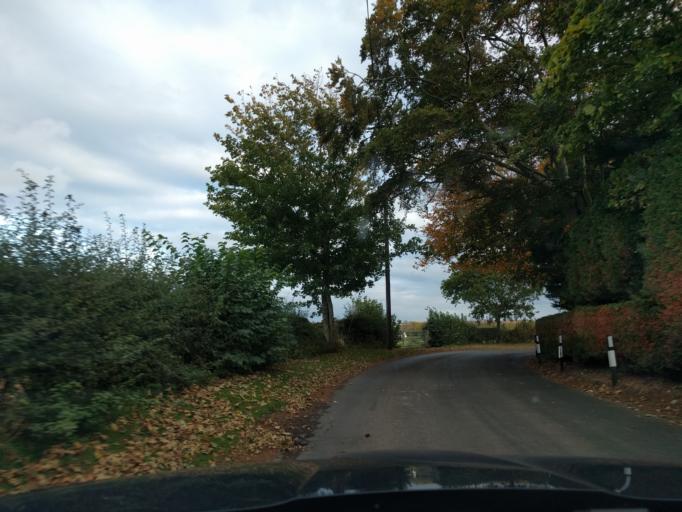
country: GB
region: England
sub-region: Northumberland
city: Ancroft
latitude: 55.7367
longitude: -2.0971
